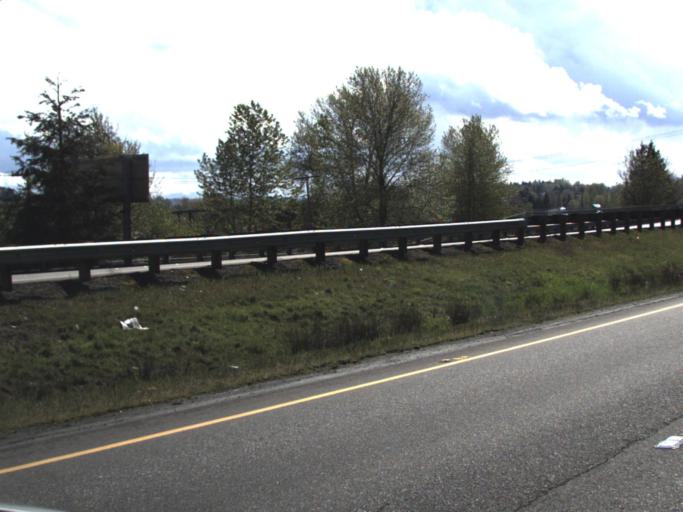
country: US
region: Washington
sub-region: King County
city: Tukwila
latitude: 47.4855
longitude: -122.2750
